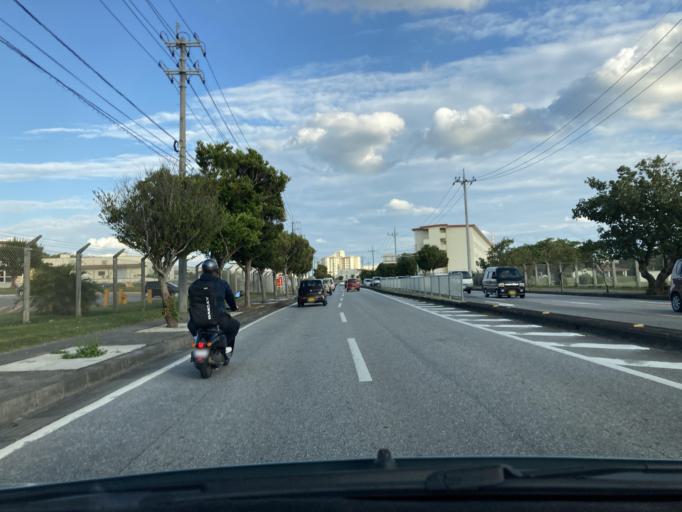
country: JP
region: Okinawa
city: Chatan
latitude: 26.3080
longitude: 127.7664
